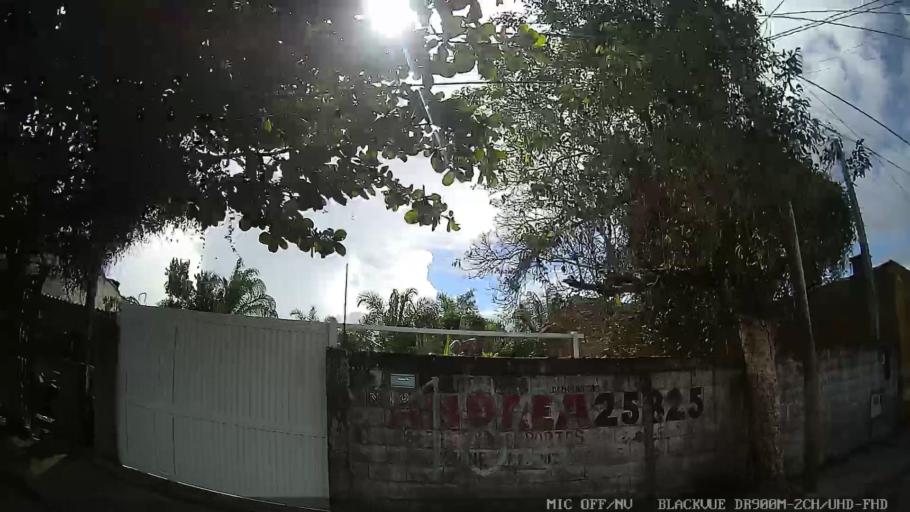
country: BR
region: Sao Paulo
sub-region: Itanhaem
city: Itanhaem
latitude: -24.2358
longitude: -46.8854
